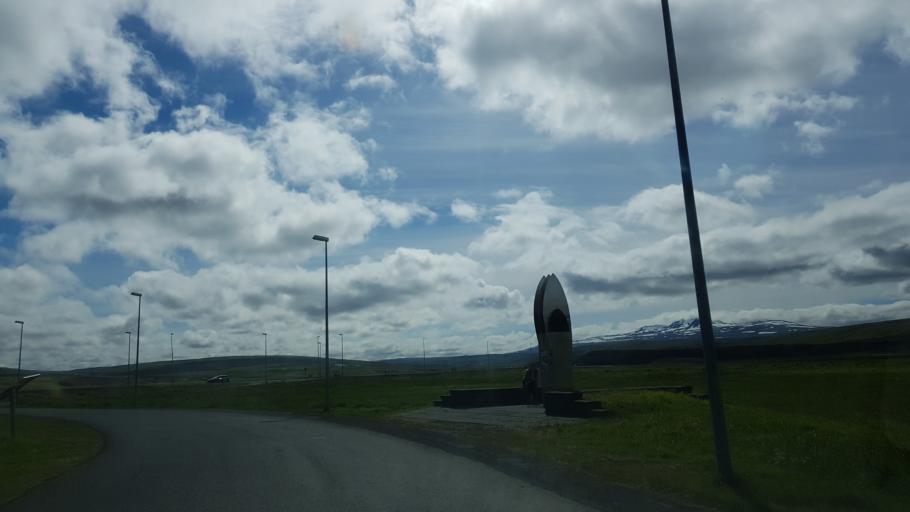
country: IS
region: West
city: Borgarnes
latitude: 65.1446
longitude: -21.0850
